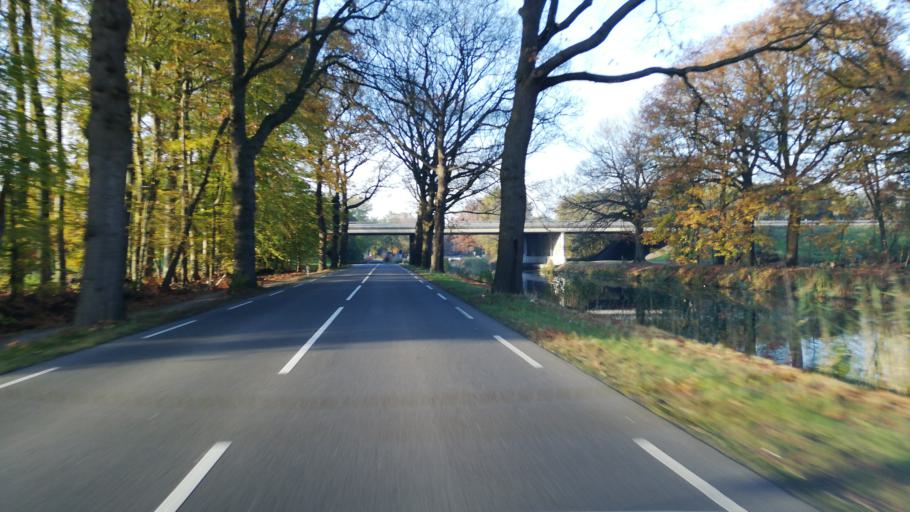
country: NL
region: Gelderland
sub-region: Gemeente Apeldoorn
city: Beekbergen
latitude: 52.1791
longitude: 5.9926
